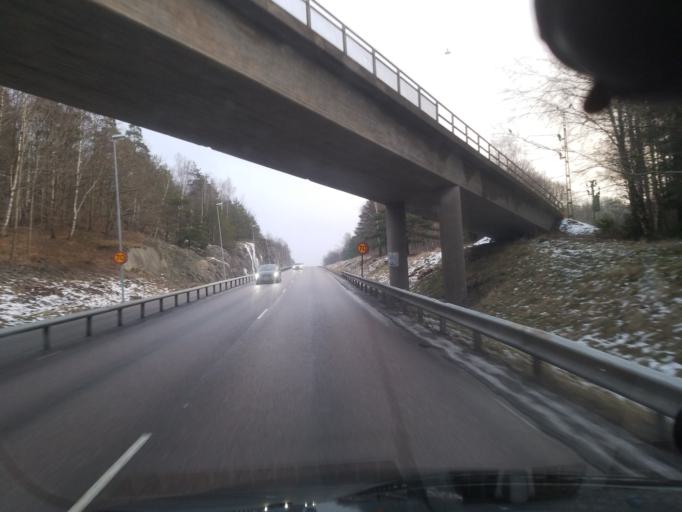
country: SE
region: Vaestra Goetaland
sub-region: Uddevalla Kommun
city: Uddevalla
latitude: 58.3541
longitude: 11.8730
